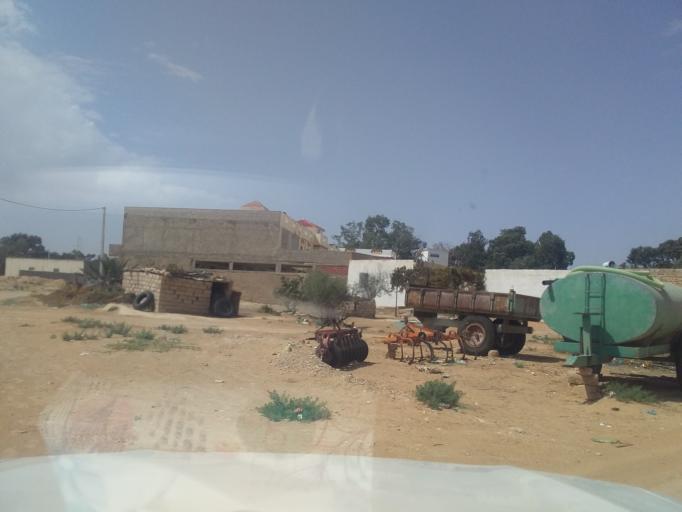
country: TN
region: Madanin
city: Medenine
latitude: 33.5822
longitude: 10.3198
